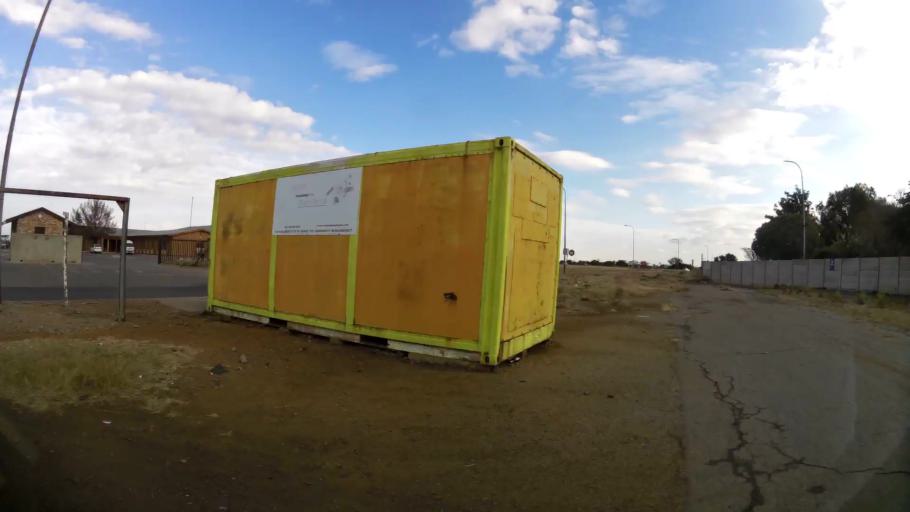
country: ZA
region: Orange Free State
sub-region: Lejweleputswa District Municipality
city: Welkom
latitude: -28.0017
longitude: 26.7374
